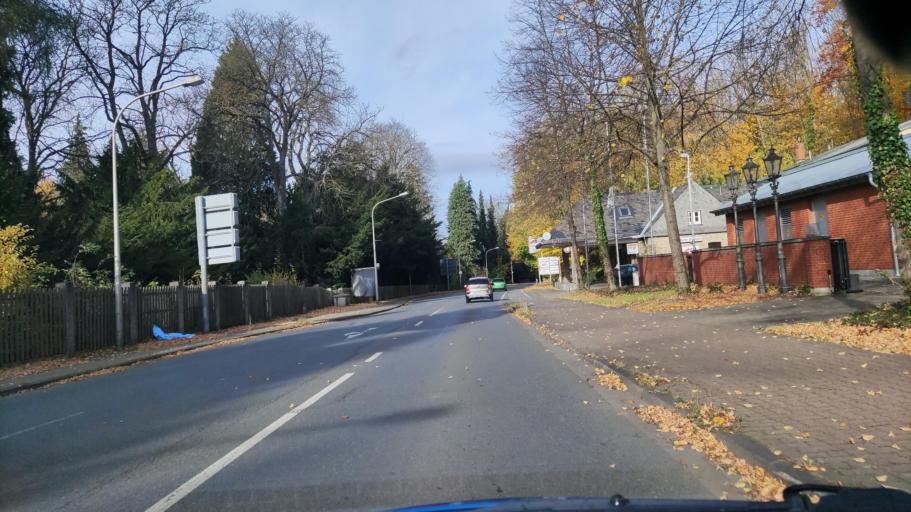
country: DE
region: Lower Saxony
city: Goslar
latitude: 51.9144
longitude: 10.4191
